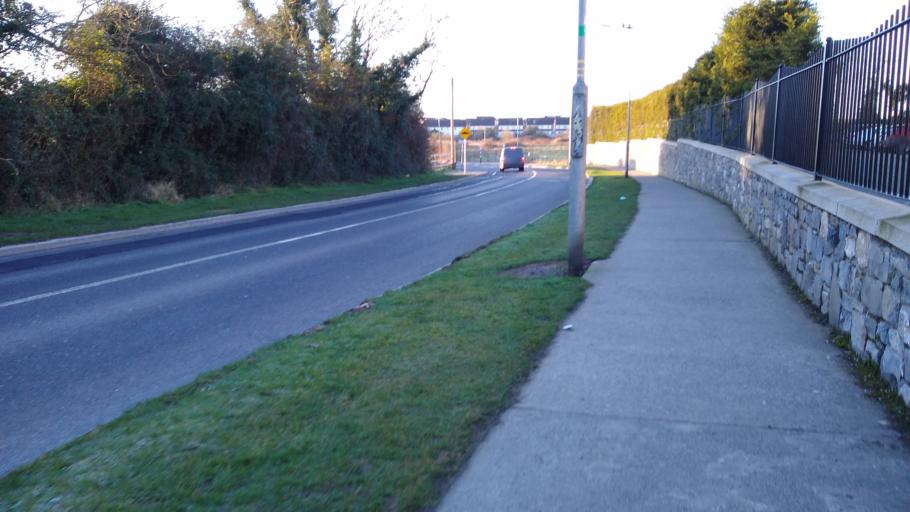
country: IE
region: Leinster
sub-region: An Mhi
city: Ashbourne
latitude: 53.5122
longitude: -6.4047
